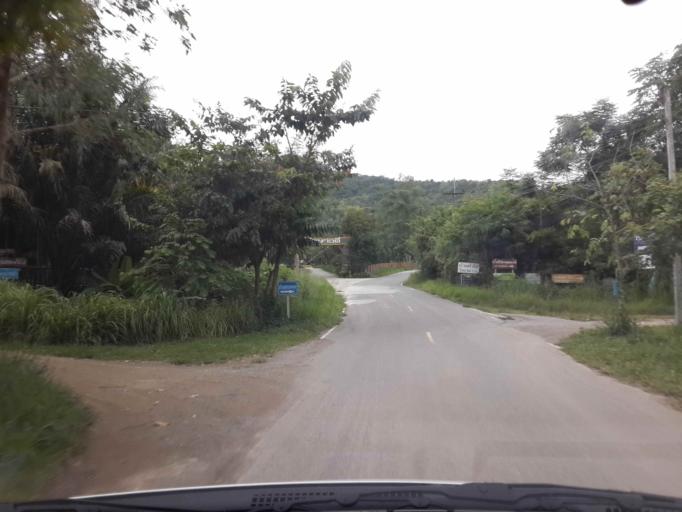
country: TH
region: Ratchaburi
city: Suan Phueng
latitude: 13.5865
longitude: 99.2181
